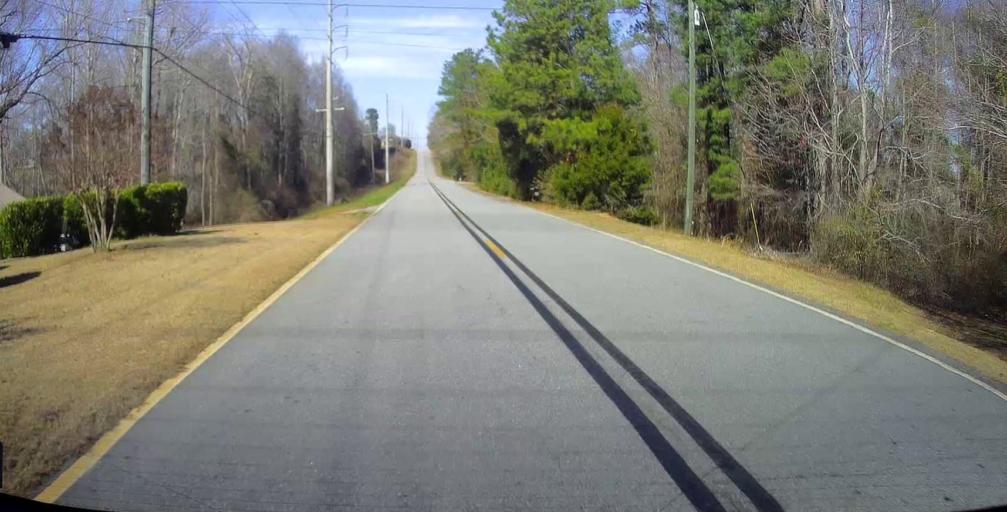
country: US
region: Georgia
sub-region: Houston County
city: Perry
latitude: 32.4688
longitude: -83.7589
